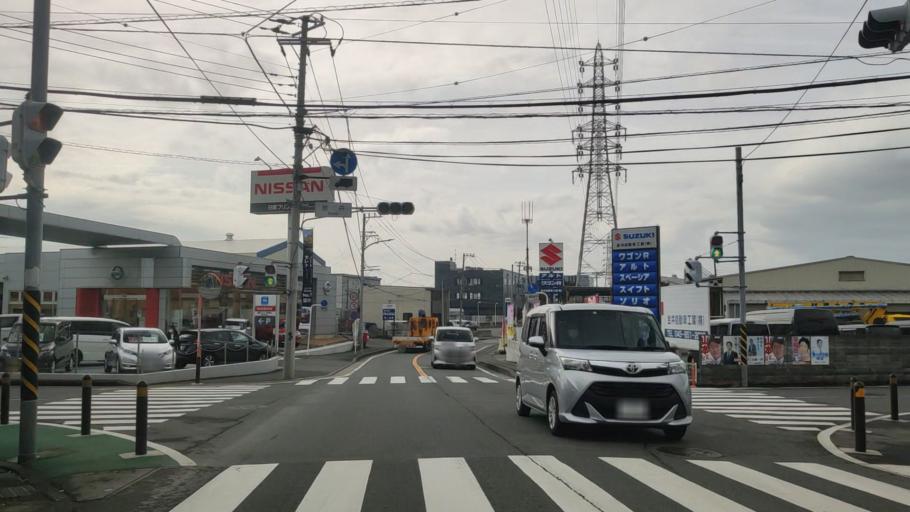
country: JP
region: Kanagawa
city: Fujisawa
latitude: 35.3787
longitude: 139.5257
